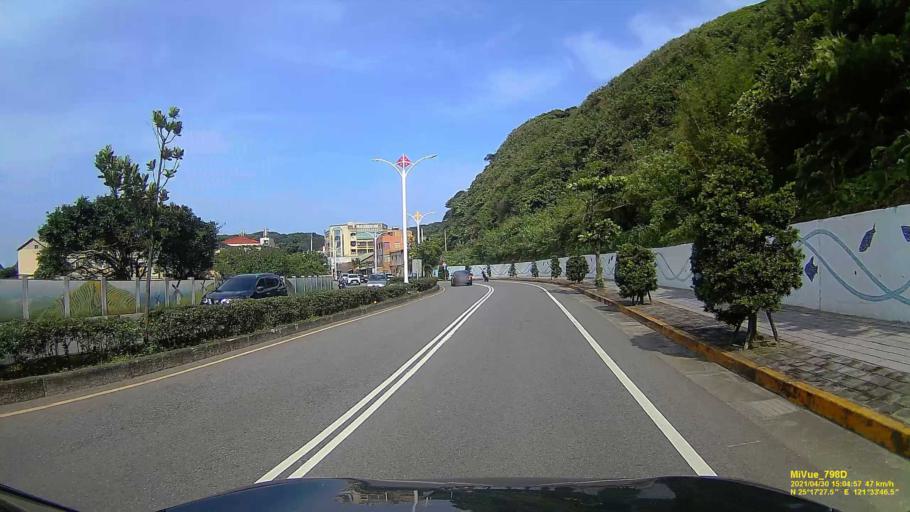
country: TW
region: Taiwan
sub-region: Keelung
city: Keelung
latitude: 25.2910
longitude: 121.5633
